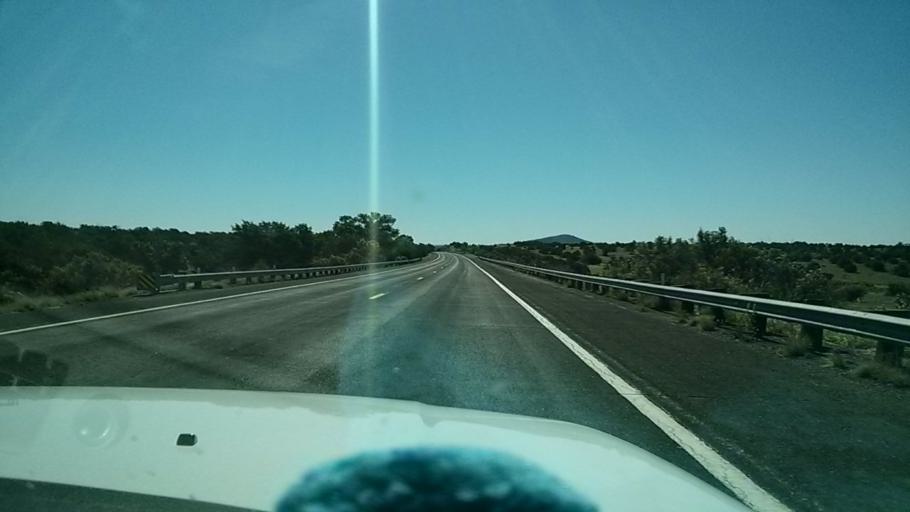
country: US
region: Arizona
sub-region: Mohave County
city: Peach Springs
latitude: 35.5532
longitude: -113.3684
